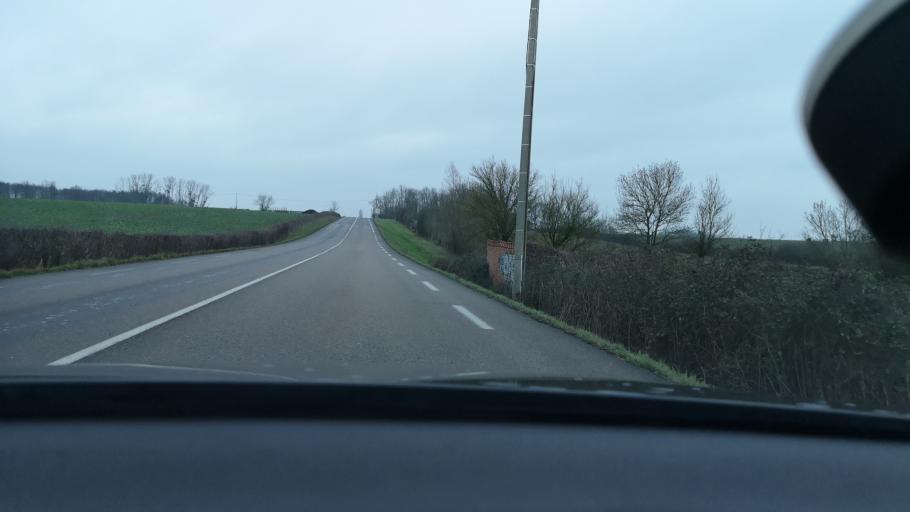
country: FR
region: Bourgogne
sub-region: Departement de la Cote-d'Or
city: Seurre
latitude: 46.9464
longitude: 5.1552
